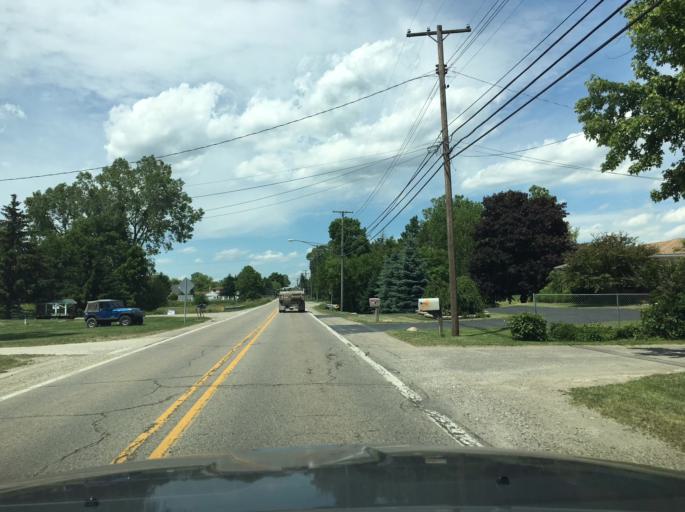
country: US
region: Michigan
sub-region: Macomb County
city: Romeo
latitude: 42.7316
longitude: -82.9600
